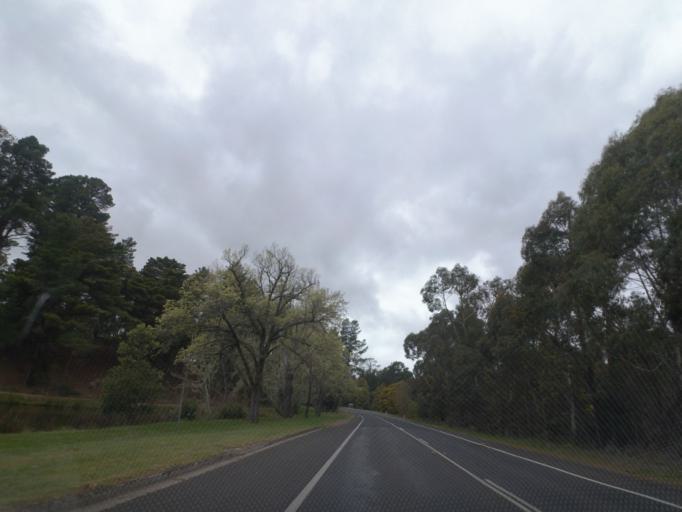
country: AU
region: Victoria
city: Brown Hill
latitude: -37.4187
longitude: 143.8999
